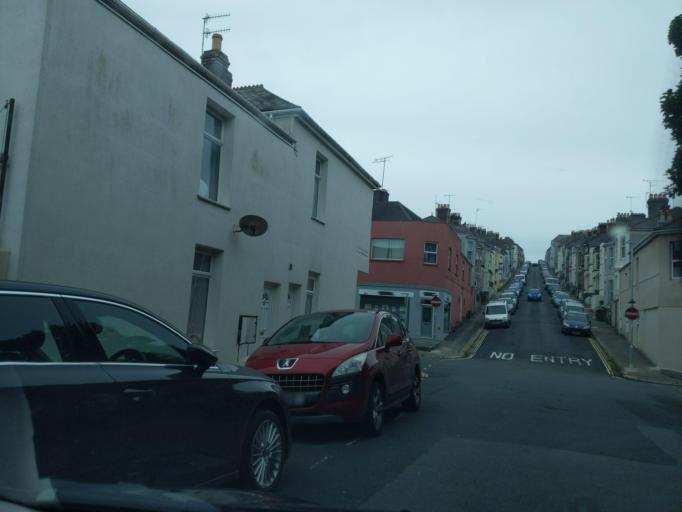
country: GB
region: England
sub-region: Cornwall
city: Millbrook
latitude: 50.3842
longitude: -4.1753
